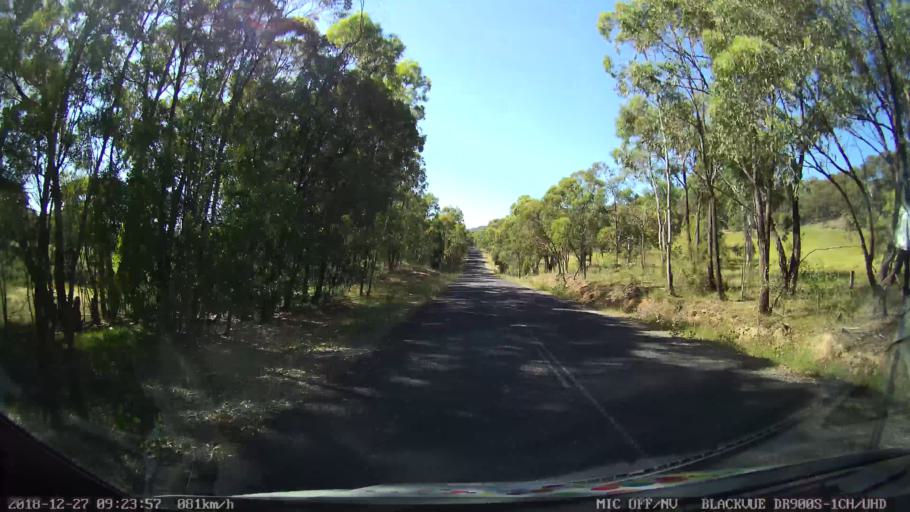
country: AU
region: New South Wales
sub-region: Lithgow
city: Portland
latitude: -33.1315
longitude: 149.9964
